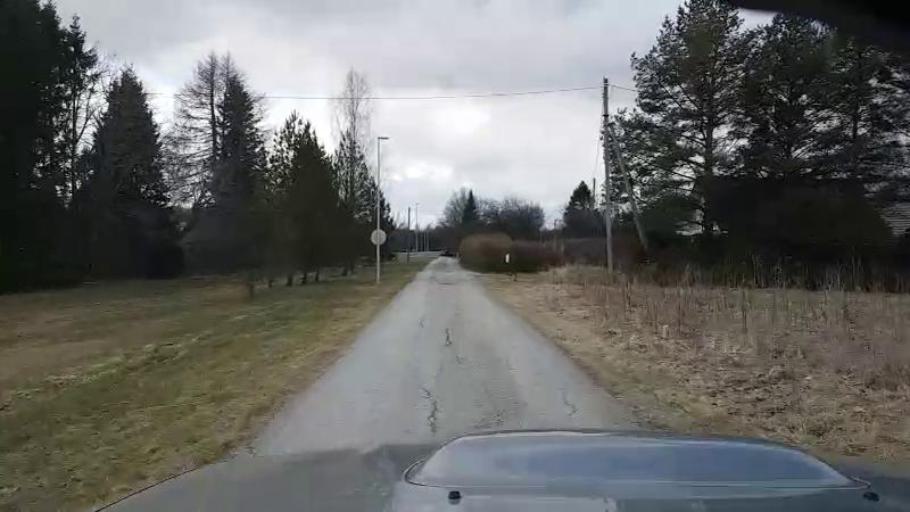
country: EE
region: Jaervamaa
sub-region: Paide linn
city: Paide
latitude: 58.9042
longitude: 25.5767
